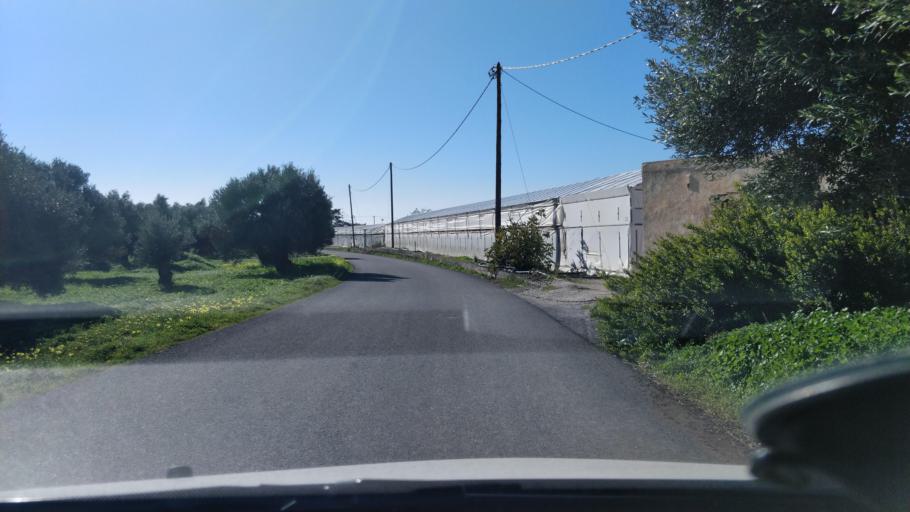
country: GR
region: Crete
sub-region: Nomos Lasithiou
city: Gra Liyia
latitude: 35.0175
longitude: 25.6762
